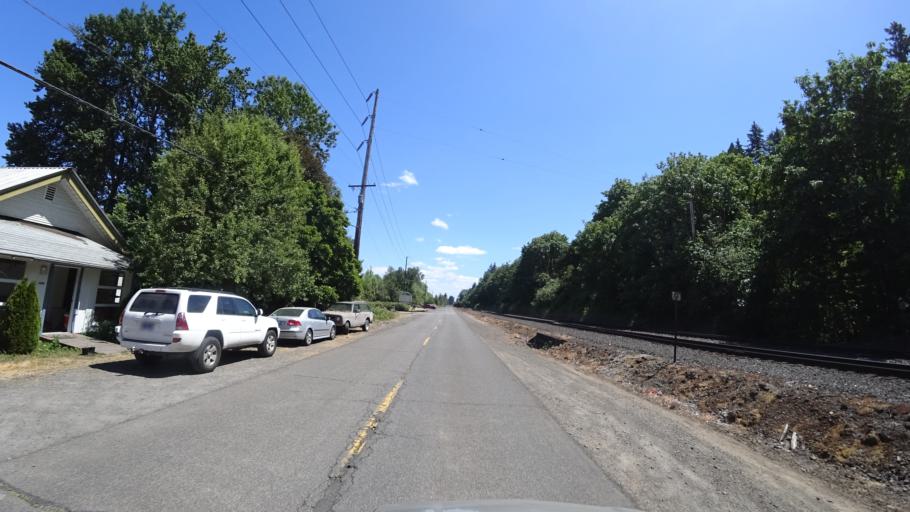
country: US
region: Oregon
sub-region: Washington County
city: Oak Hills
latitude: 45.6183
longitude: -122.8066
